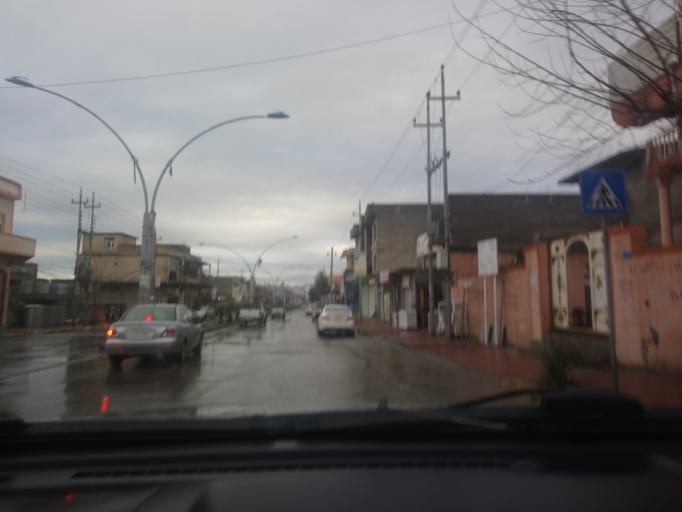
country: IQ
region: As Sulaymaniyah
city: Qeladize
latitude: 36.1798
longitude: 45.1343
